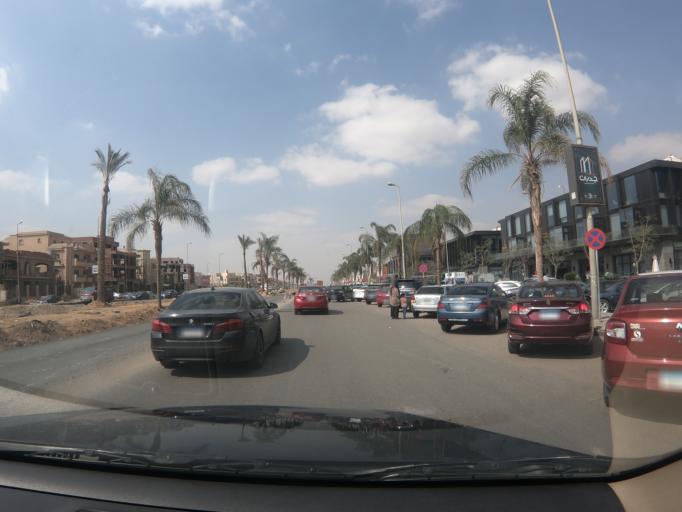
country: EG
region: Muhafazat al Qalyubiyah
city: Al Khankah
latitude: 30.0401
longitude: 31.4750
